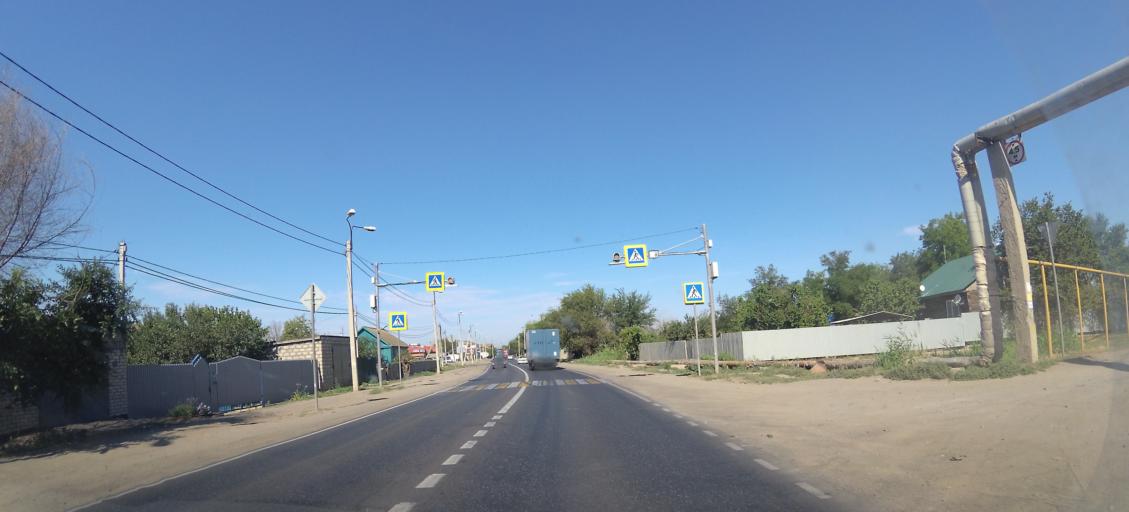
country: RU
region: Volgograd
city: Novyy Rogachik
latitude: 48.6793
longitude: 44.0587
